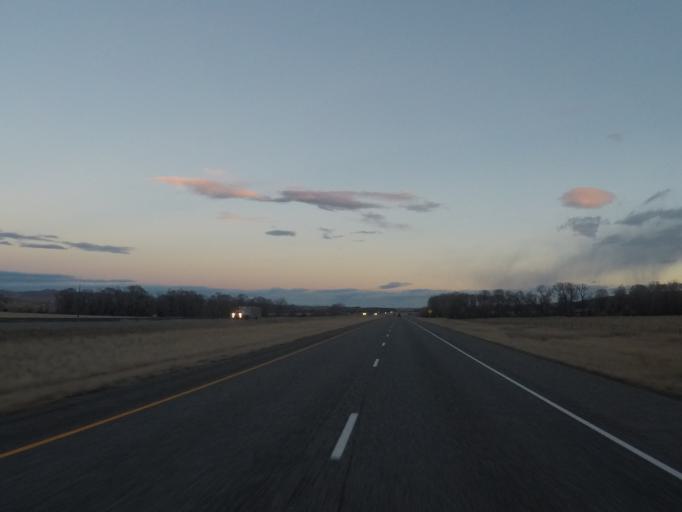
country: US
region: Montana
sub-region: Sweet Grass County
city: Big Timber
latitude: 45.7956
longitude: -109.8384
